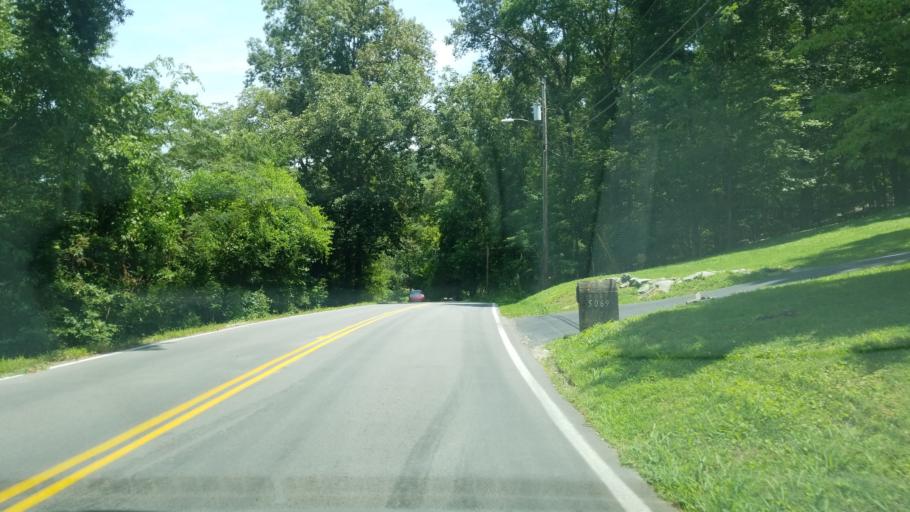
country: US
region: Tennessee
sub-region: Hamilton County
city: East Chattanooga
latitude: 35.1262
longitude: -85.2141
